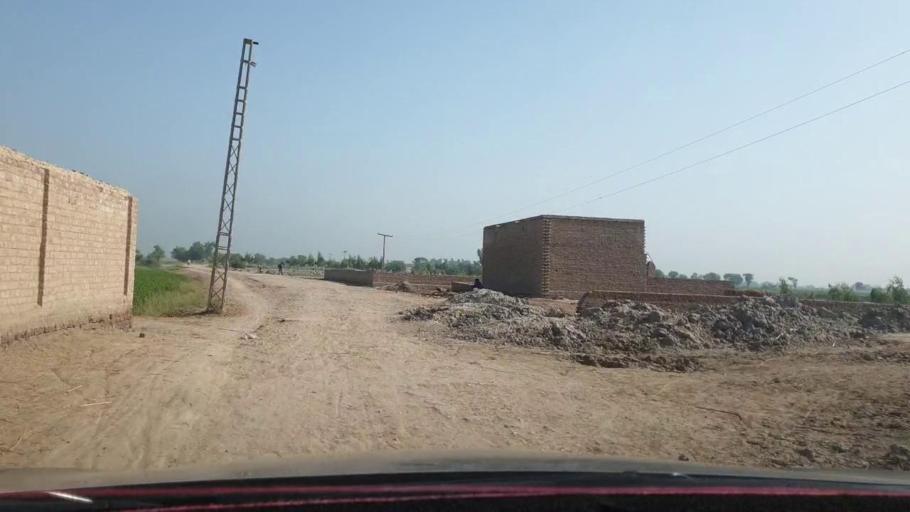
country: PK
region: Sindh
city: Nasirabad
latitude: 27.4542
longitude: 67.9175
